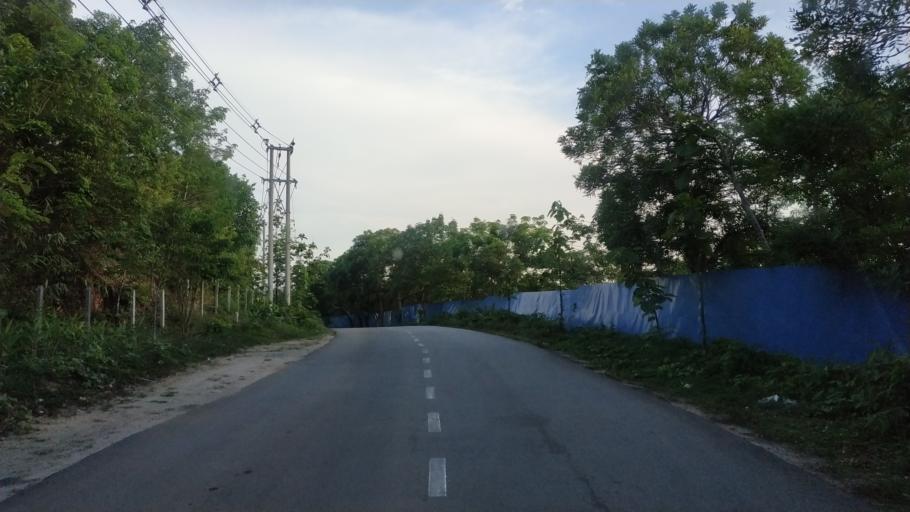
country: MM
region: Mon
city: Kyaikto
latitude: 17.4176
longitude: 97.0709
